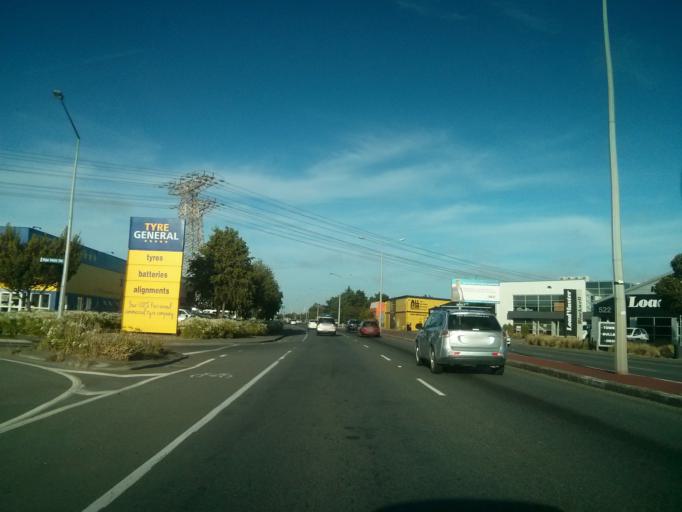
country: NZ
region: Canterbury
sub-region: Selwyn District
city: Prebbleton
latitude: -43.5392
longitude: 172.5604
